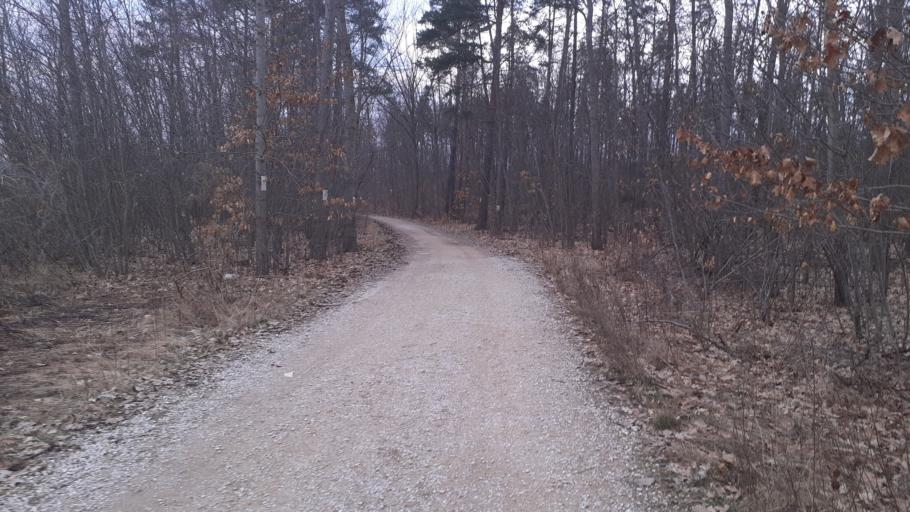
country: DE
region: Bavaria
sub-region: Regierungsbezirk Mittelfranken
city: Feucht
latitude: 49.4116
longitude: 11.1768
